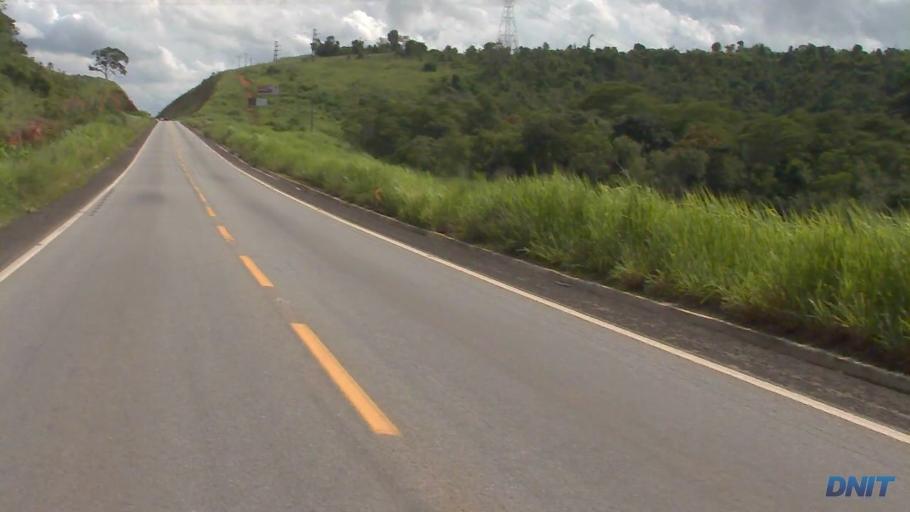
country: BR
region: Minas Gerais
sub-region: Ipatinga
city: Ipatinga
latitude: -19.4139
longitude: -42.4911
